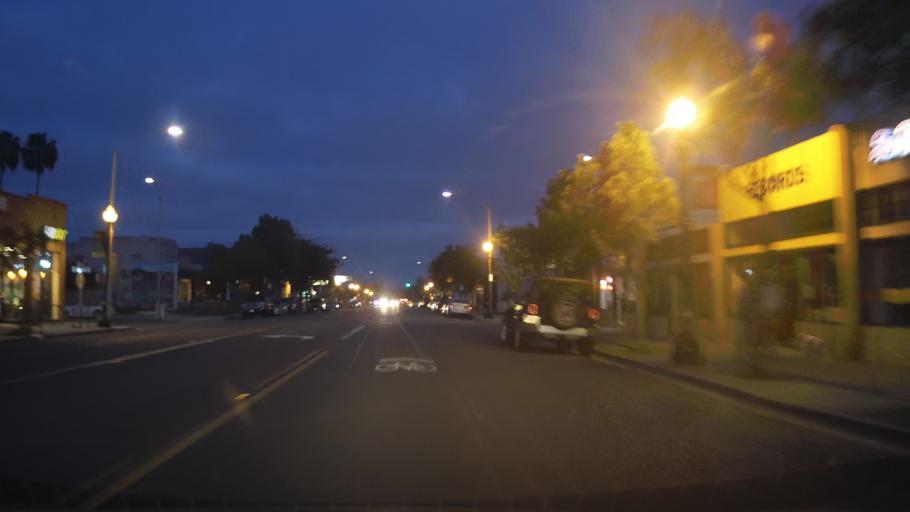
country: US
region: California
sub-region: San Diego County
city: San Diego
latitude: 32.7633
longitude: -117.1167
